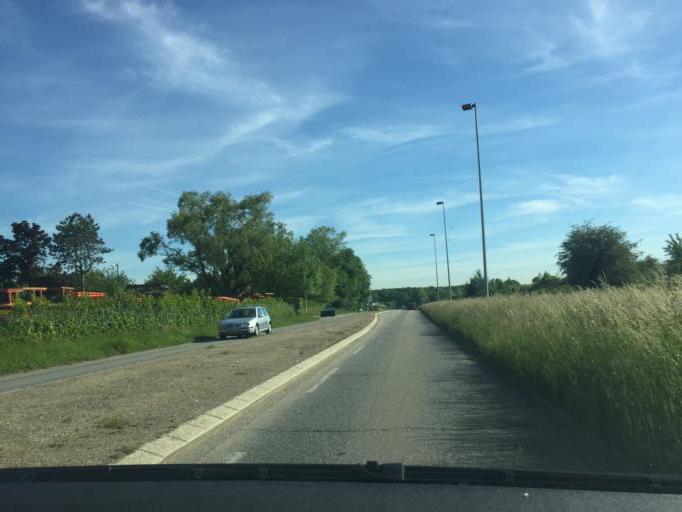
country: FR
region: Ile-de-France
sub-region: Departement des Yvelines
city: Buc
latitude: 48.7624
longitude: 2.1260
